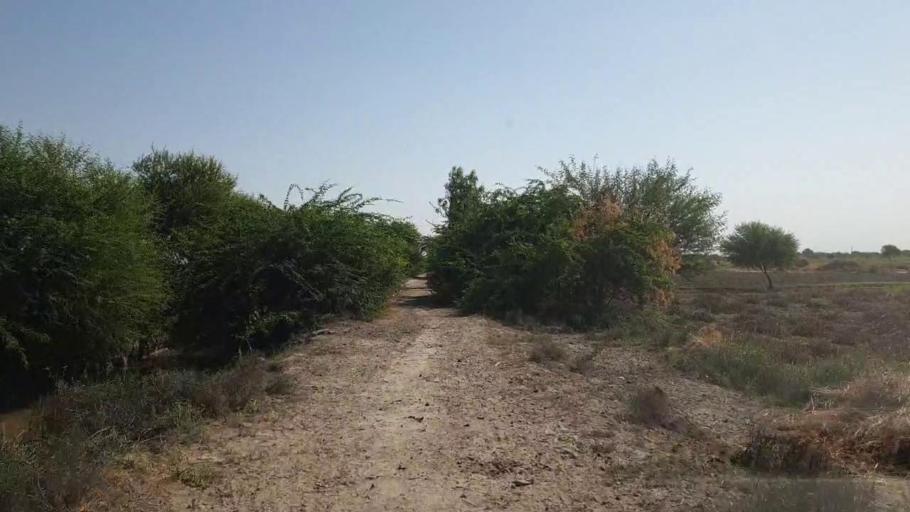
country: PK
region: Sindh
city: Kadhan
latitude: 24.5936
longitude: 69.0067
